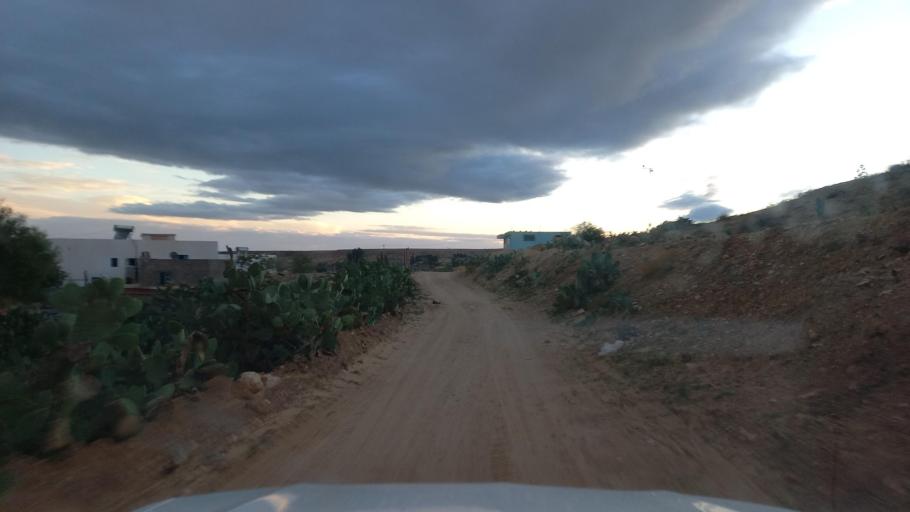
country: TN
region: Al Qasrayn
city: Kasserine
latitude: 35.2574
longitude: 8.9356
